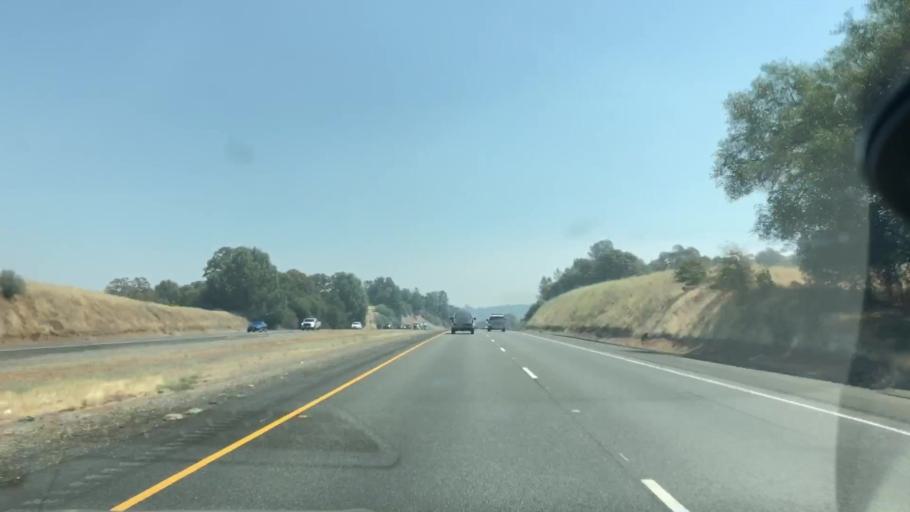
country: US
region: California
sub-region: El Dorado County
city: Shingle Springs
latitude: 38.6939
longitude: -120.8958
